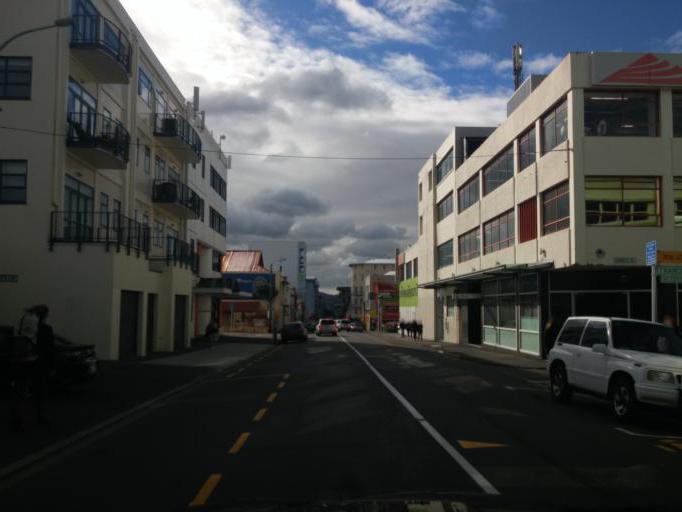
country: NZ
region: Wellington
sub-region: Wellington City
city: Wellington
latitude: -41.2977
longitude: 174.7788
